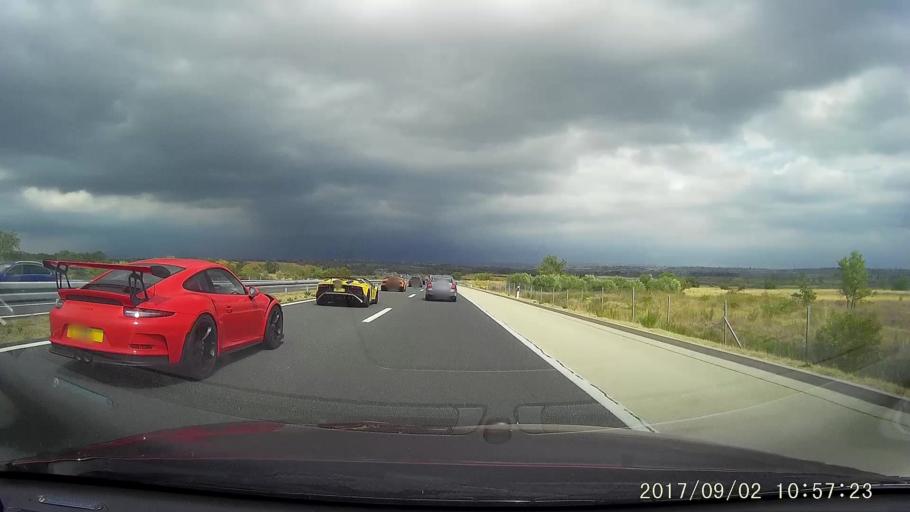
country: HR
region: Zadarska
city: Policnik
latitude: 44.1469
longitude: 15.4209
